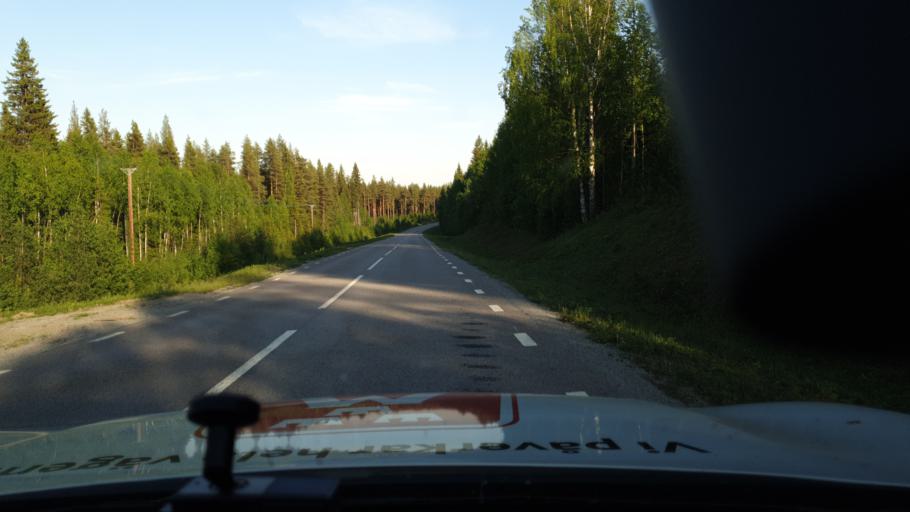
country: SE
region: Vaesterbotten
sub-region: Bjurholms Kommun
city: Bjurholm
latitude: 64.1873
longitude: 18.8939
